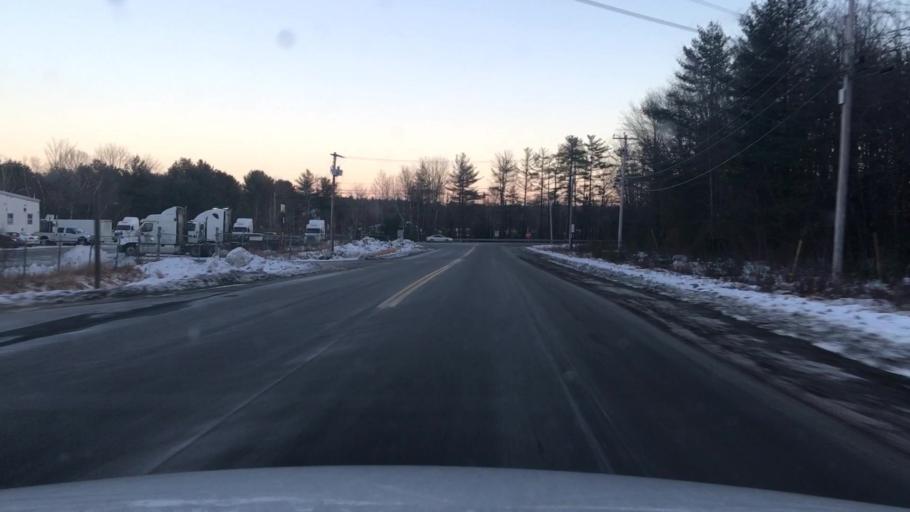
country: US
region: Maine
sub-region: Androscoggin County
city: Auburn
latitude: 44.0700
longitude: -70.2499
